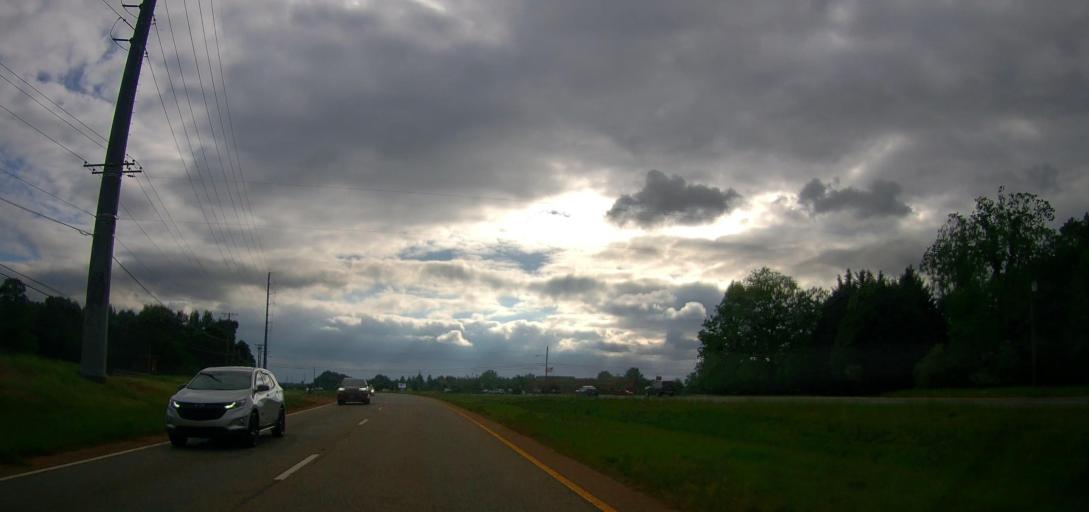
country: US
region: Georgia
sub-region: Oconee County
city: Bogart
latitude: 33.9174
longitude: -83.5483
